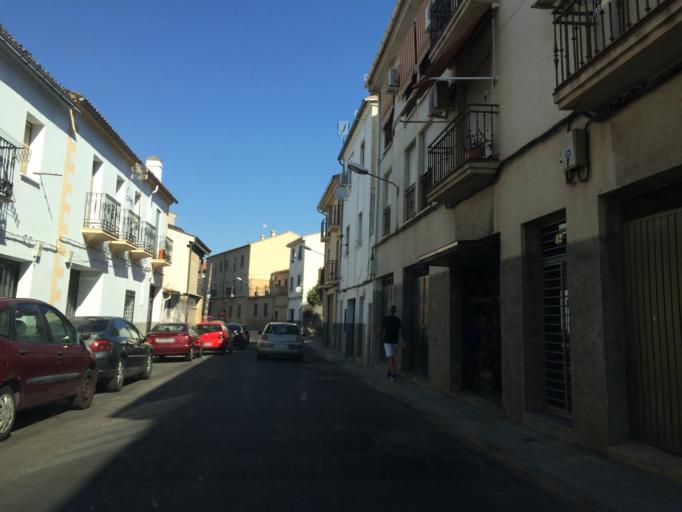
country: ES
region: Extremadura
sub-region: Provincia de Caceres
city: Plasencia
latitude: 40.0279
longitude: -6.0945
